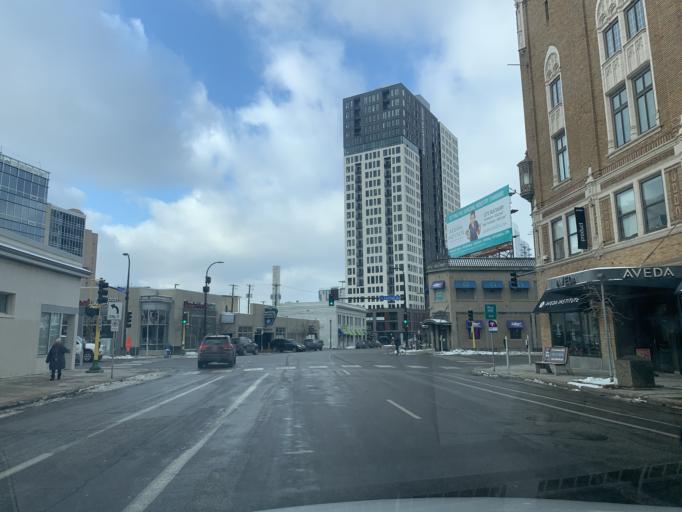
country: US
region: Minnesota
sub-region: Hennepin County
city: Minneapolis
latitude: 44.9876
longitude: -93.2536
